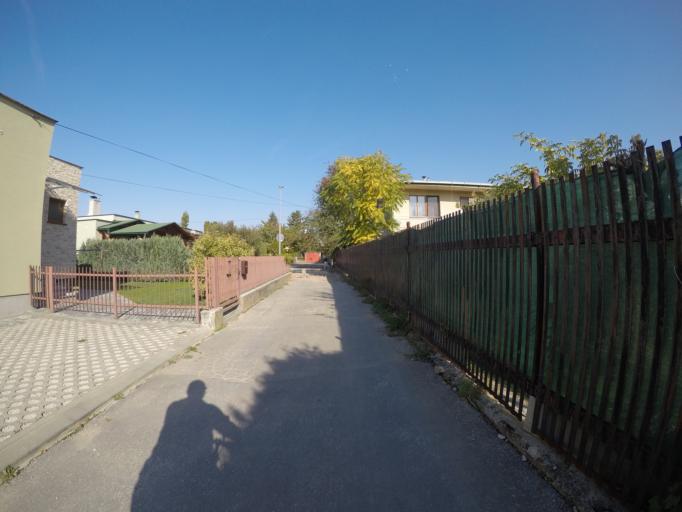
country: SK
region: Trenciansky
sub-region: Okres Nove Mesto nad Vahom
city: Nove Mesto nad Vahom
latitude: 48.7562
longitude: 17.8199
